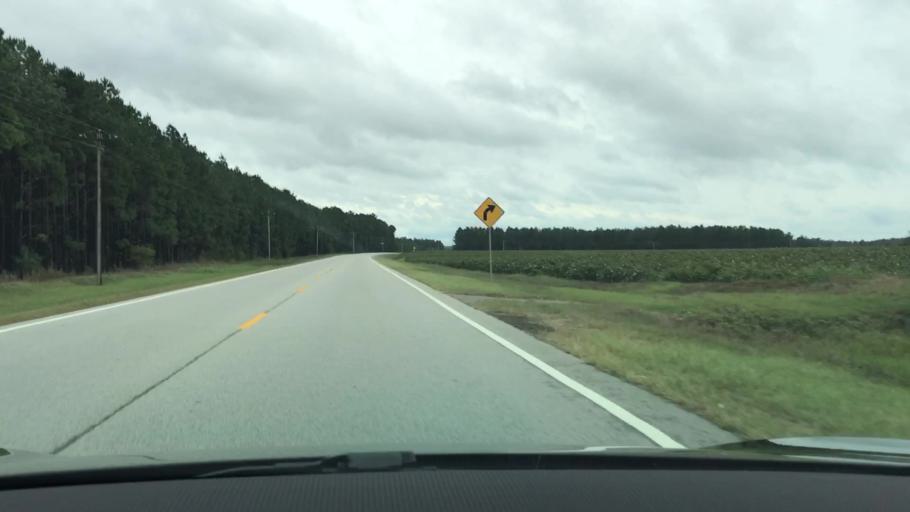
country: US
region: Georgia
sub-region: Glascock County
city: Gibson
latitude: 33.2877
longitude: -82.5077
